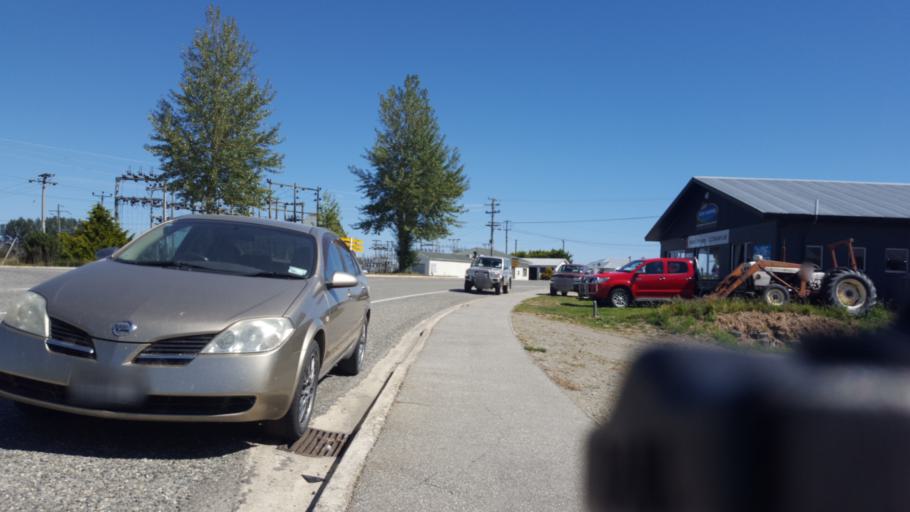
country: NZ
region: Otago
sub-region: Dunedin City
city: Dunedin
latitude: -45.1262
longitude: 170.0956
